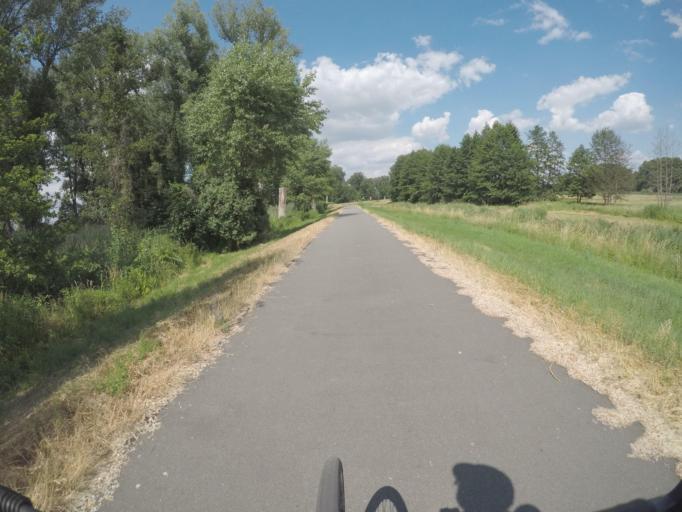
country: DE
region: Brandenburg
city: Roskow
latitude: 52.4354
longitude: 12.6611
